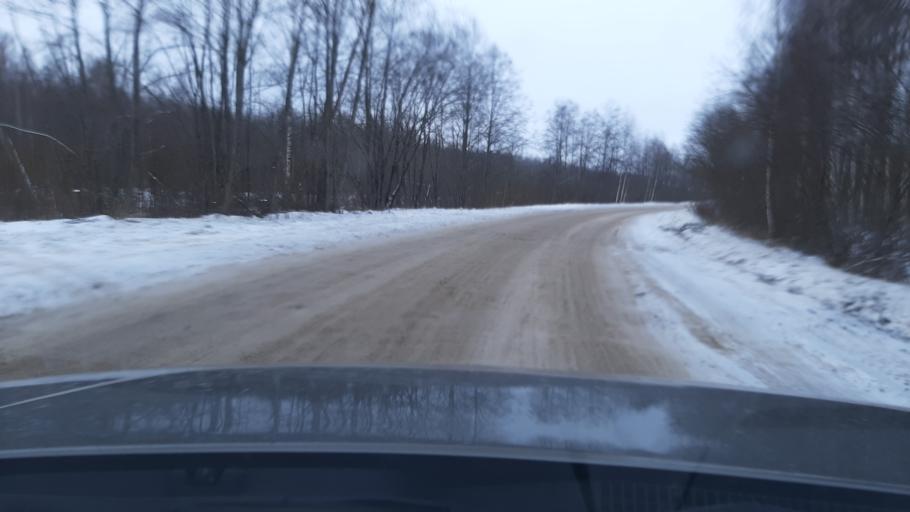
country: RU
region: Kostroma
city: Volgorechensk
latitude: 57.4420
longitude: 41.1259
